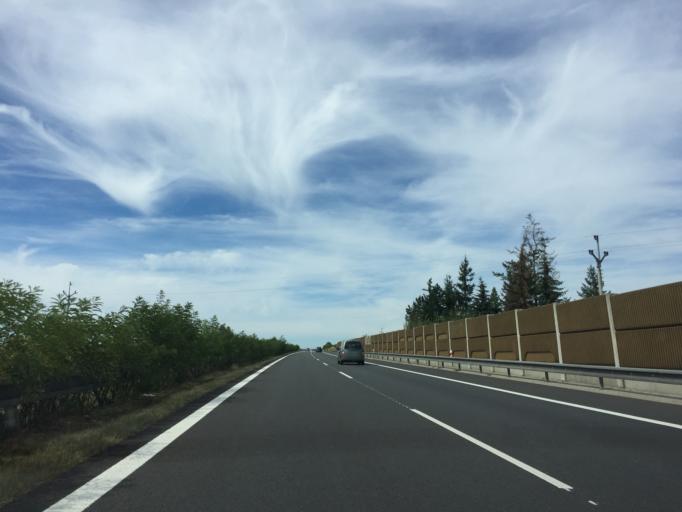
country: CZ
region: Jihocesky
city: Chotoviny
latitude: 49.4490
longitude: 14.6700
